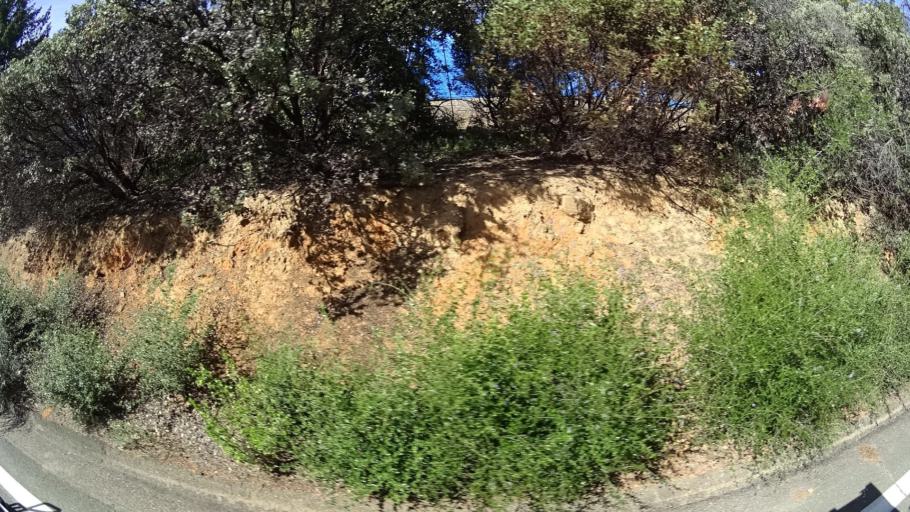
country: US
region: California
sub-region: Lake County
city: Kelseyville
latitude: 38.9088
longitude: -122.7945
